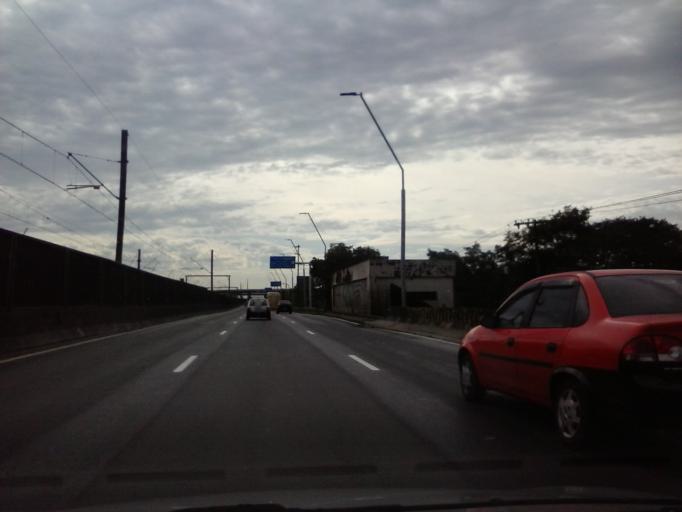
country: BR
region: Rio Grande do Sul
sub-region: Porto Alegre
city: Porto Alegre
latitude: -30.0026
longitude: -51.2079
